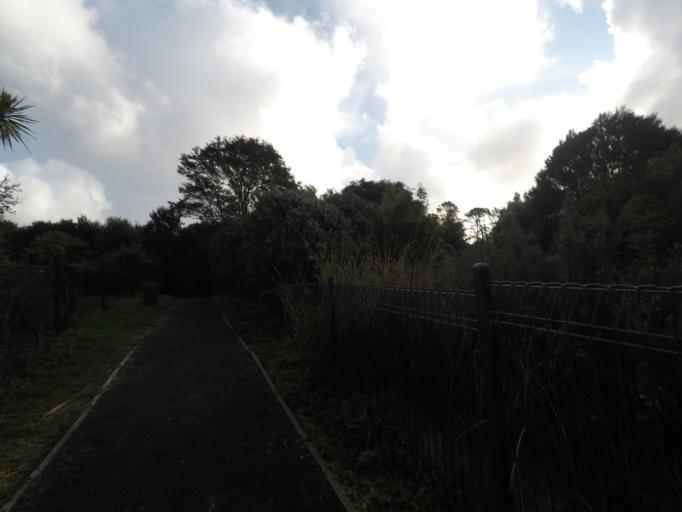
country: NZ
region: Auckland
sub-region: Auckland
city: Waitakere
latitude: -36.9035
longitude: 174.6346
